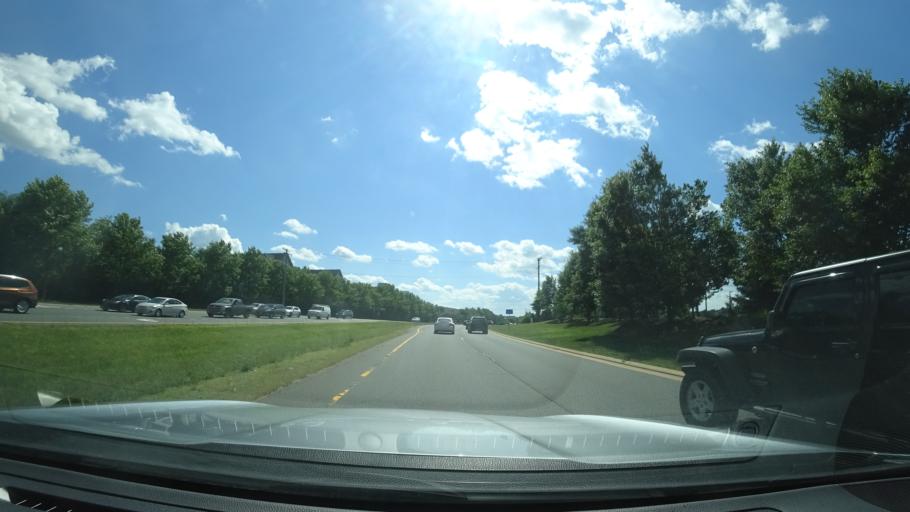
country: US
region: Virginia
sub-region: Loudoun County
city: Broadlands
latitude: 38.9953
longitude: -77.4831
